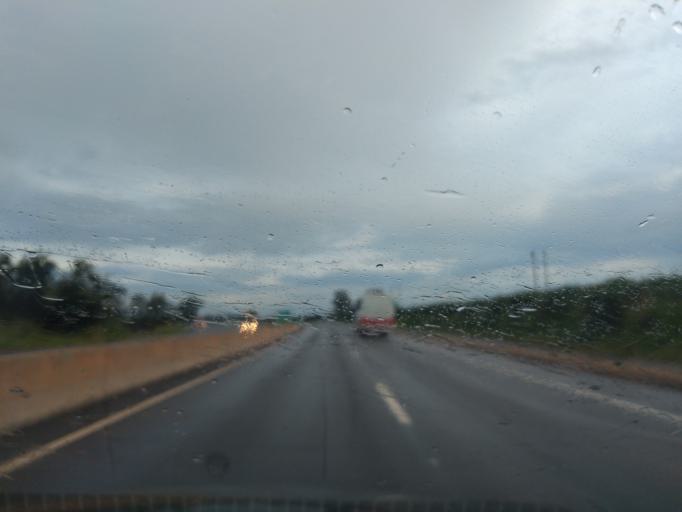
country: BR
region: Minas Gerais
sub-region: Tres Coracoes
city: Tres Coracoes
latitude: -21.6531
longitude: -45.3556
